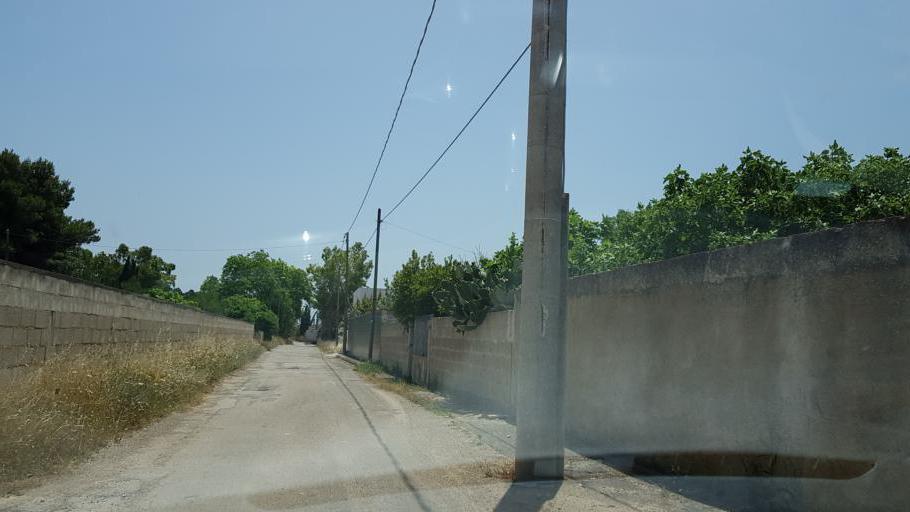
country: IT
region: Apulia
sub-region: Provincia di Lecce
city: Porto Cesareo
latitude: 40.2500
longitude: 17.9219
